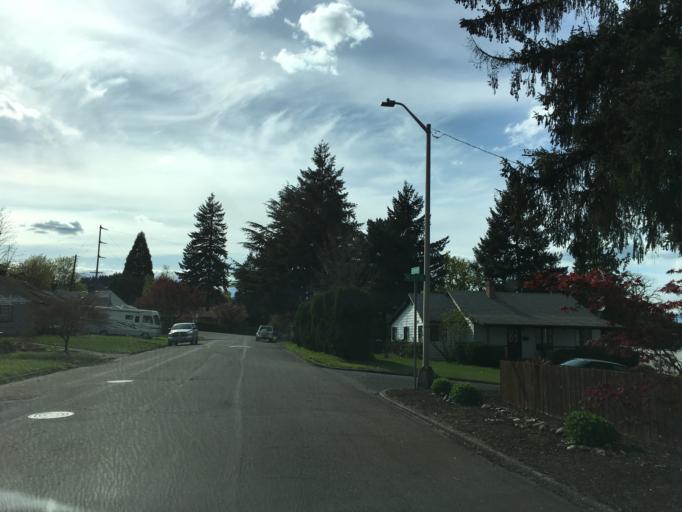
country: US
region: Oregon
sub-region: Multnomah County
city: Lents
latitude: 45.5485
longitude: -122.5461
